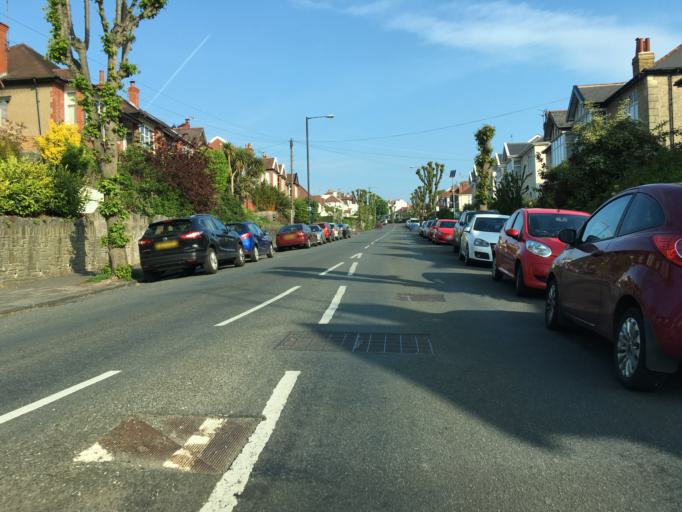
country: GB
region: England
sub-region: Bristol
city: Bristol
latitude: 51.4764
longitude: -2.6030
